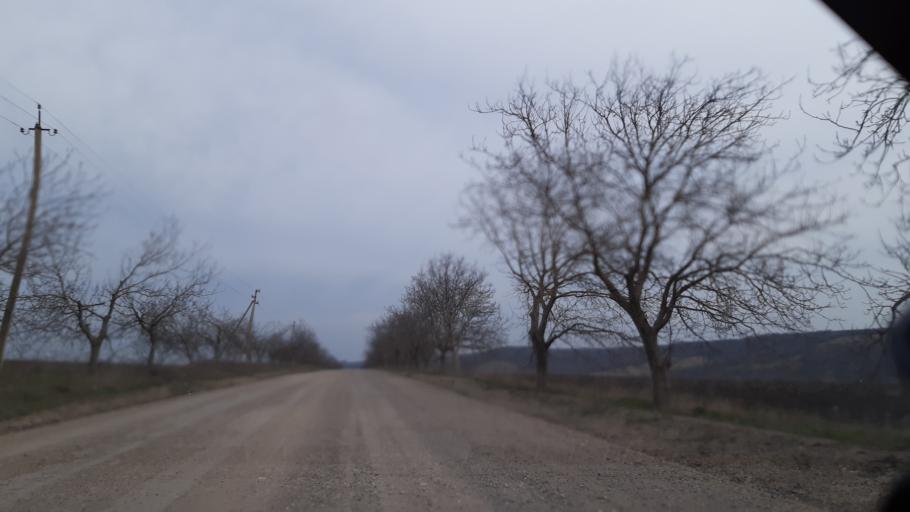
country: MD
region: Soldanesti
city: Soldanesti
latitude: 47.6938
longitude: 28.7350
